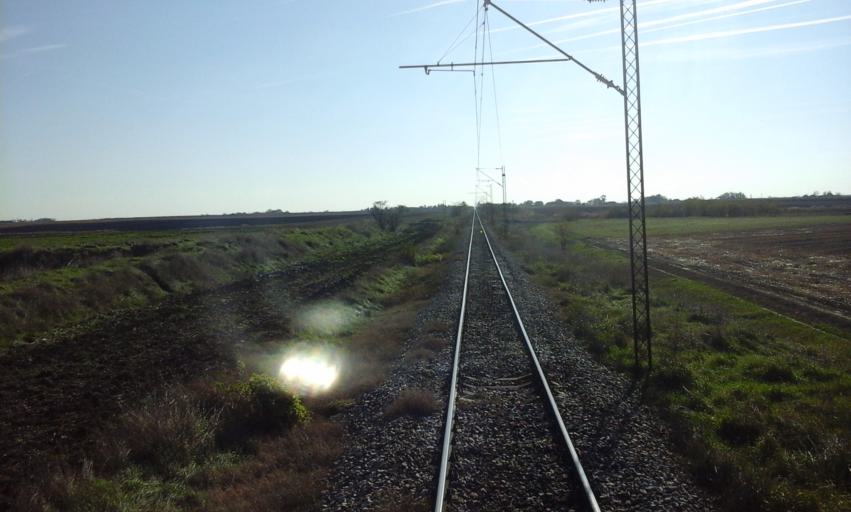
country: RS
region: Autonomna Pokrajina Vojvodina
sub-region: Severnobacki Okrug
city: Subotica
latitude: 45.9996
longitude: 19.6775
